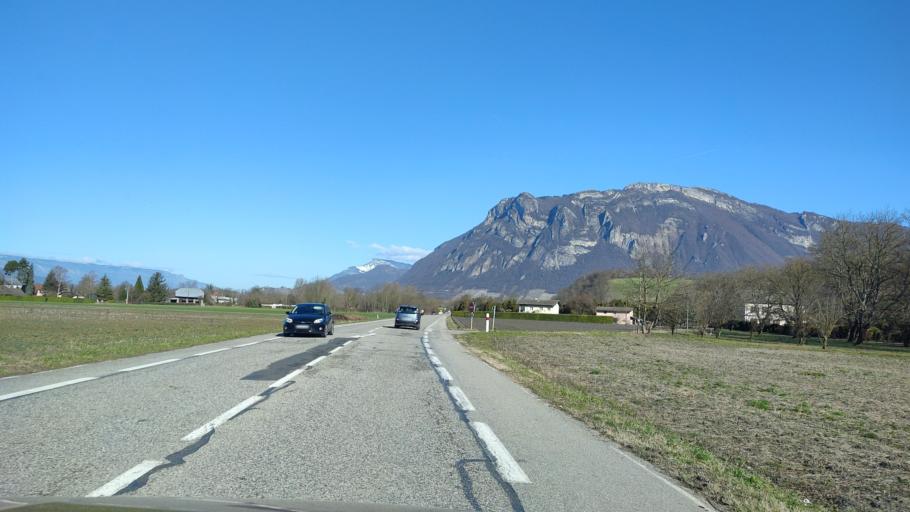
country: FR
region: Rhone-Alpes
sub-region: Departement de la Savoie
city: Montmelian
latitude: 45.4727
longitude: 6.0429
